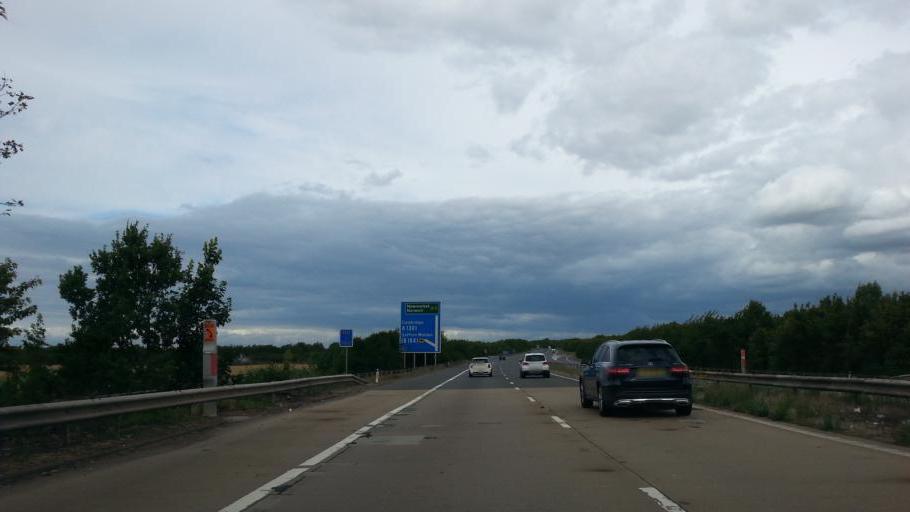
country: GB
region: England
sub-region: Cambridgeshire
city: Duxford
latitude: 52.0700
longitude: 0.1879
